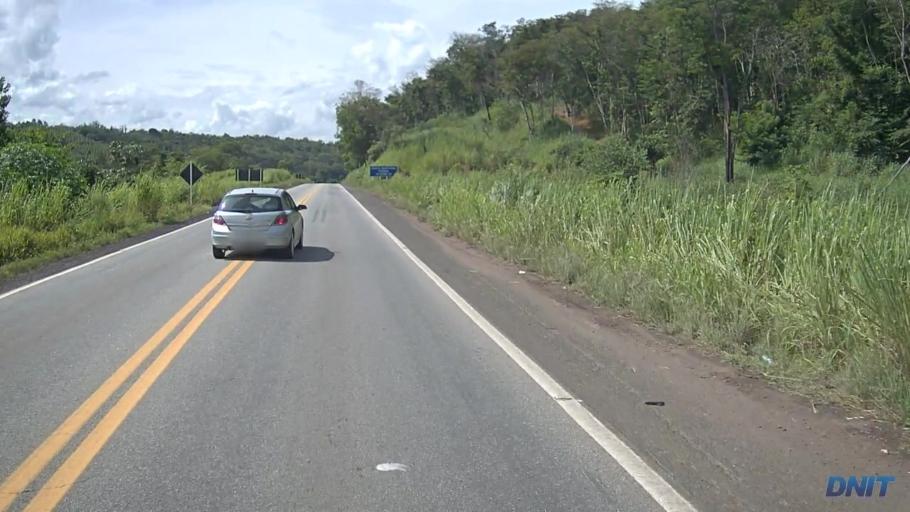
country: BR
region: Minas Gerais
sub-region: Ipaba
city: Ipaba
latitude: -19.4015
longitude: -42.4835
